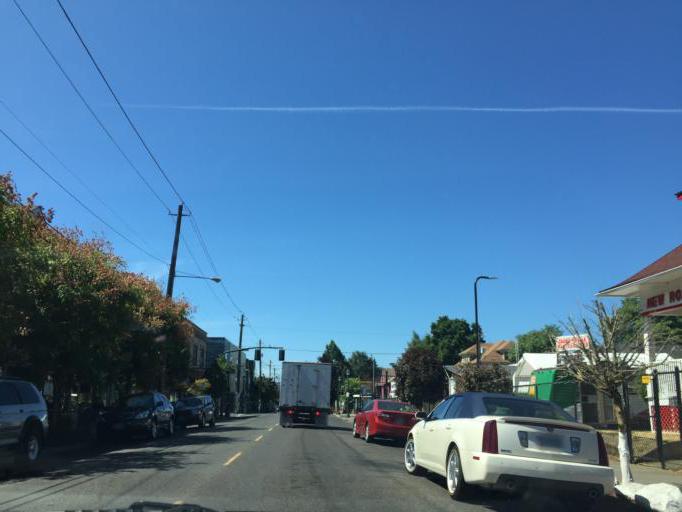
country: US
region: Oregon
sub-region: Multnomah County
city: Portland
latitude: 45.5591
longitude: -122.6488
